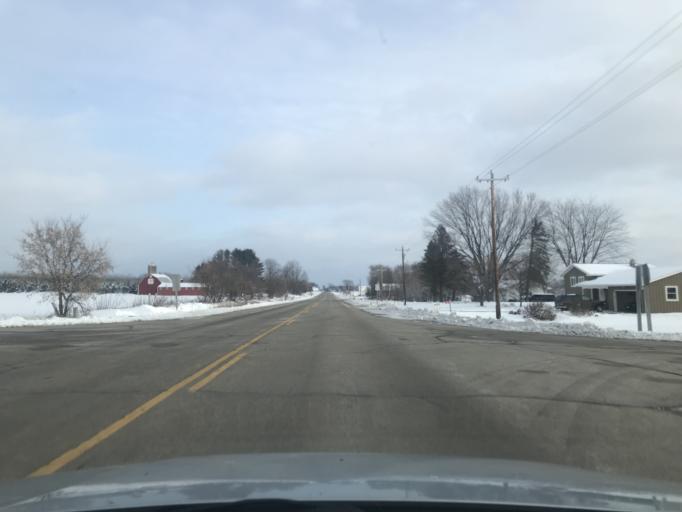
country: US
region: Wisconsin
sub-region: Oconto County
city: Oconto
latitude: 44.8928
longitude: -87.9688
